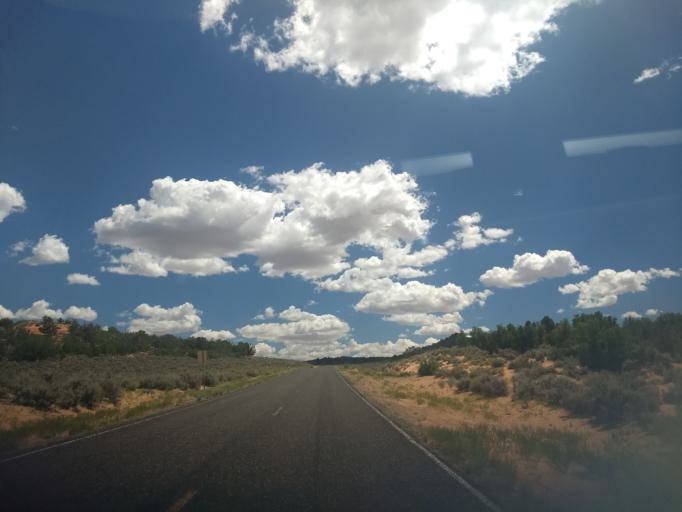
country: US
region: Utah
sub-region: Kane County
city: Kanab
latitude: 37.1418
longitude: -112.6753
